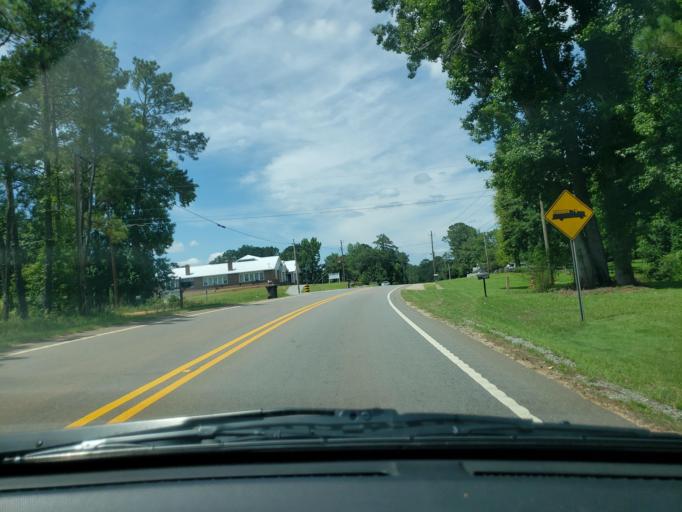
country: US
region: Alabama
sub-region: Elmore County
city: Eclectic
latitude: 32.6762
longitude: -85.9446
